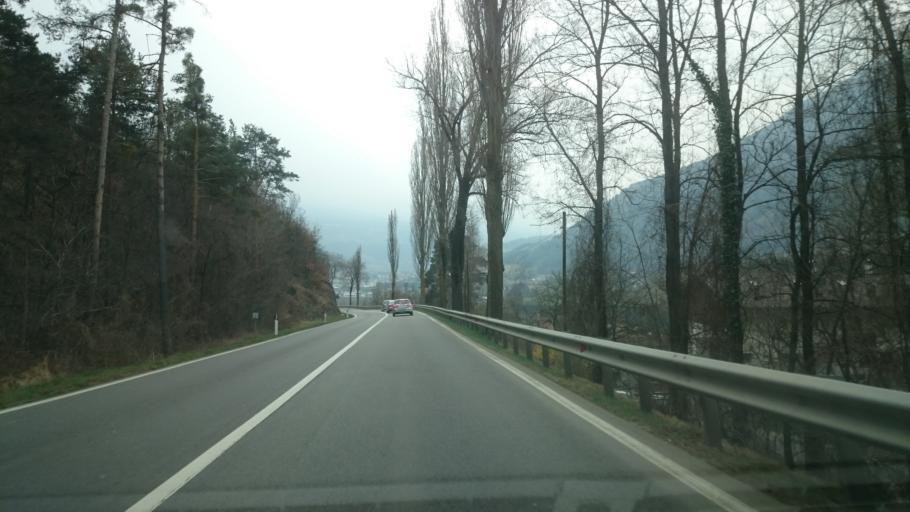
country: IT
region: Trentino-Alto Adige
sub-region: Bolzano
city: Varna
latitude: 46.7497
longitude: 11.6472
